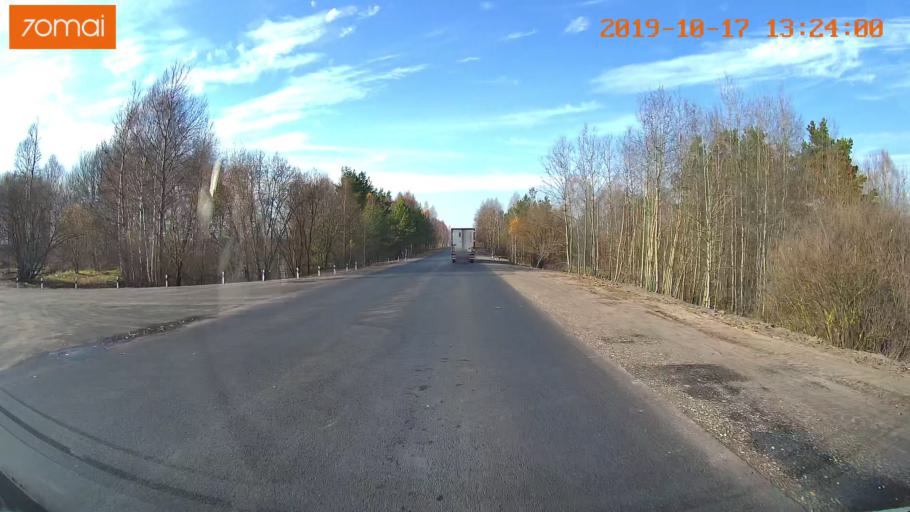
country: RU
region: Rjazan
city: Gus'-Zheleznyy
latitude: 55.0927
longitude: 40.9706
